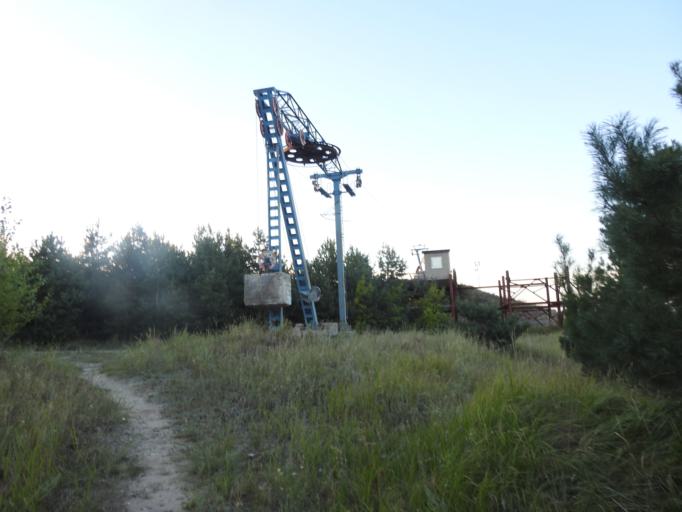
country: RU
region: Saratov
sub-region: Saratovskiy Rayon
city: Saratov
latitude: 51.5564
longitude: 45.9757
